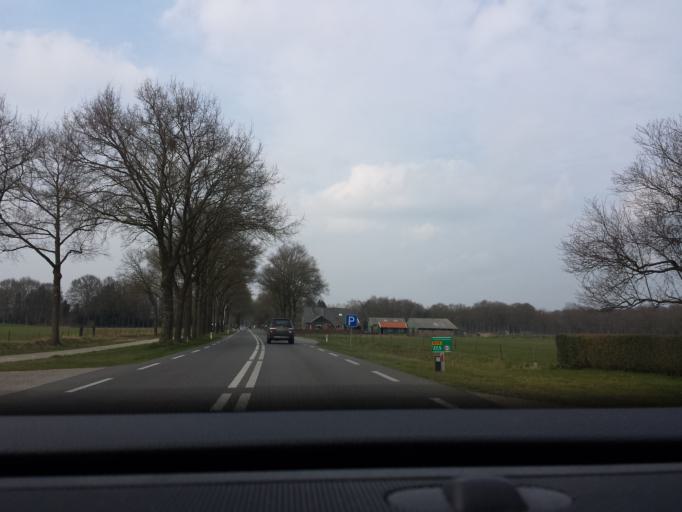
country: NL
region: Gelderland
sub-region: Gemeente Bronckhorst
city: Hengelo
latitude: 52.0885
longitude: 6.3162
